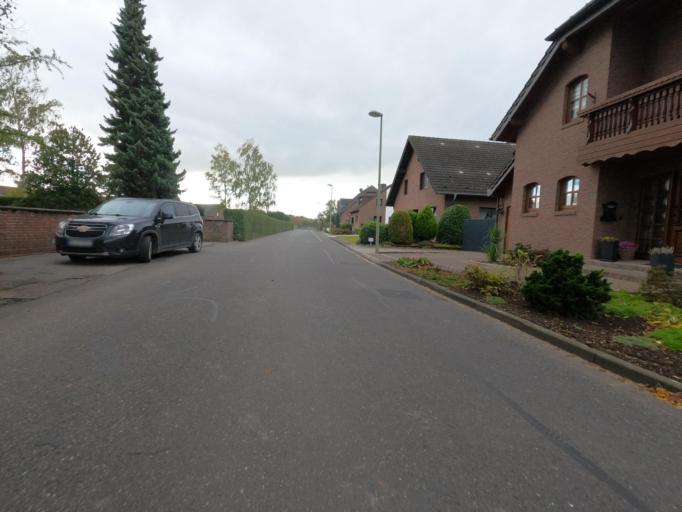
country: DE
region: North Rhine-Westphalia
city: Erkelenz
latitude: 51.0568
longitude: 6.2751
